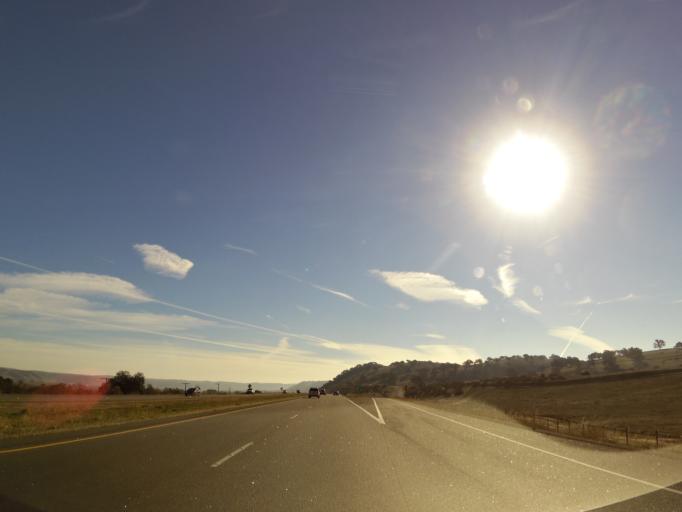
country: US
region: California
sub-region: San Luis Obispo County
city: Lake Nacimiento
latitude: 35.8663
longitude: -120.8216
